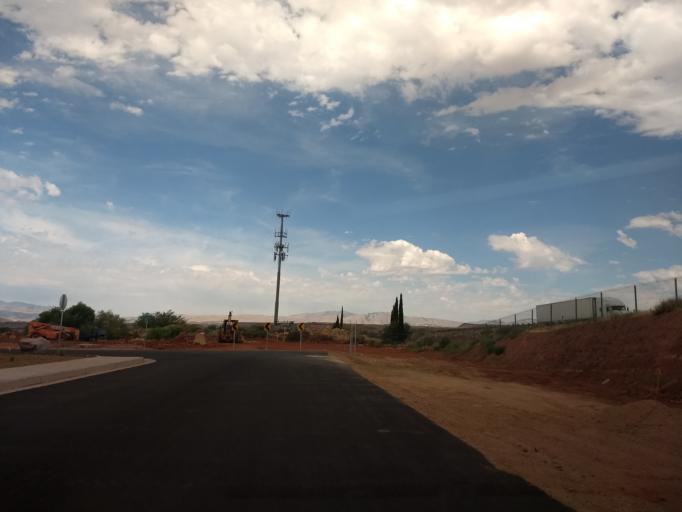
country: US
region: Utah
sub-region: Washington County
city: Washington
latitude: 37.1421
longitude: -113.4994
